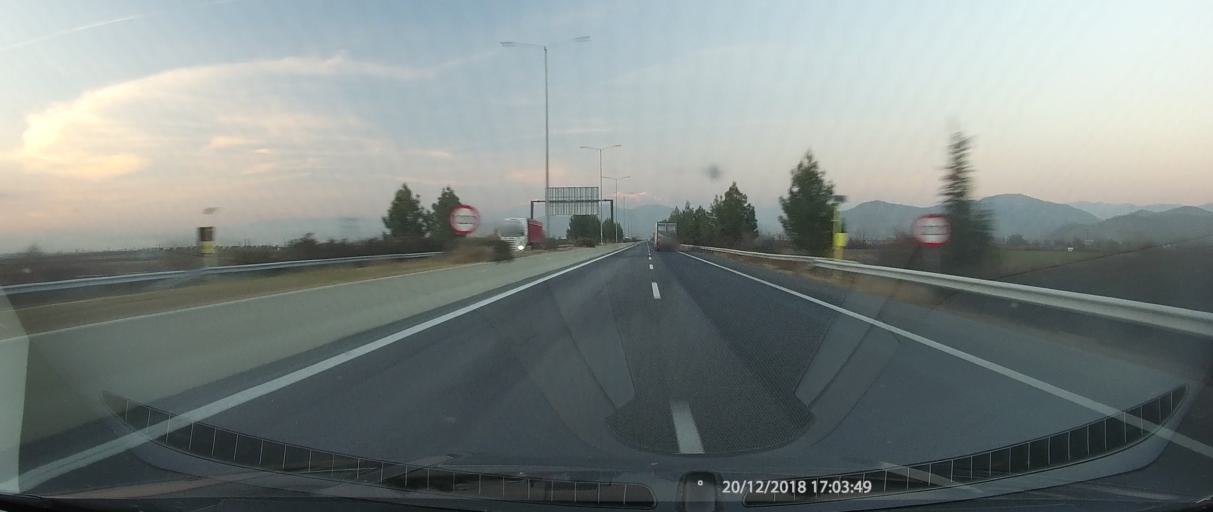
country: GR
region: Thessaly
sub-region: Nomos Larisis
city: Falani
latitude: 39.7047
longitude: 22.4857
